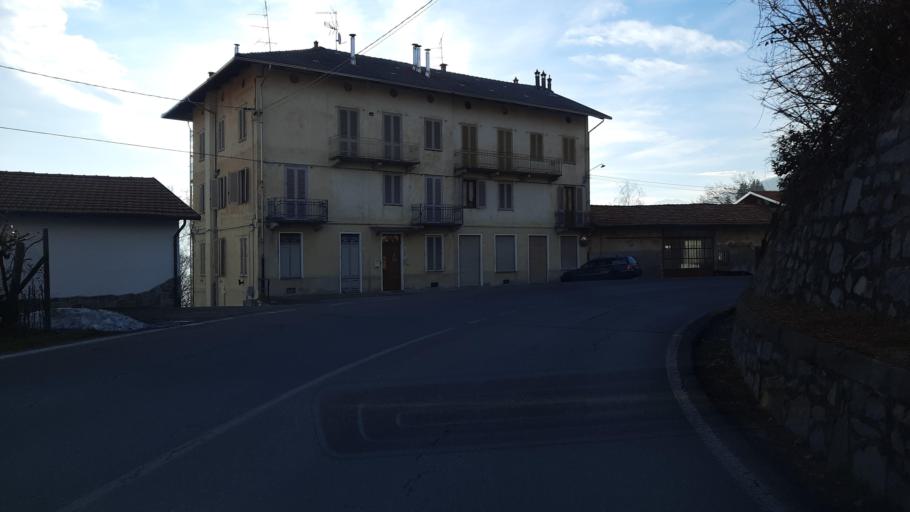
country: IT
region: Piedmont
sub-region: Provincia di Biella
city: Mosso
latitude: 45.6488
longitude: 8.1458
